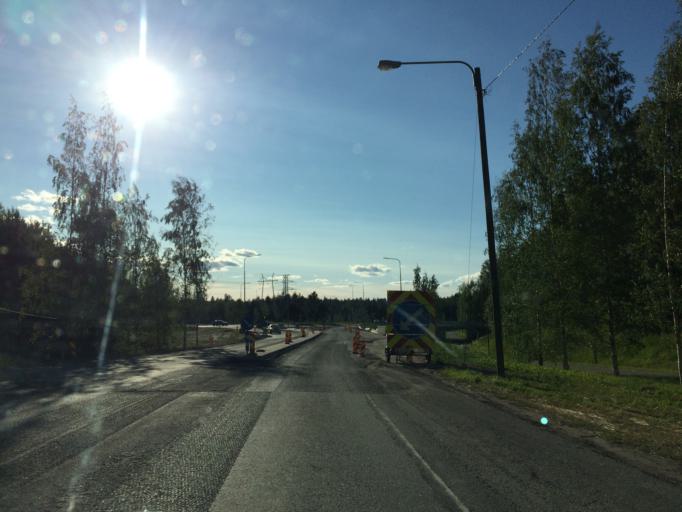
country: FI
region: Haeme
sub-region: Haemeenlinna
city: Haemeenlinna
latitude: 60.9833
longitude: 24.5101
